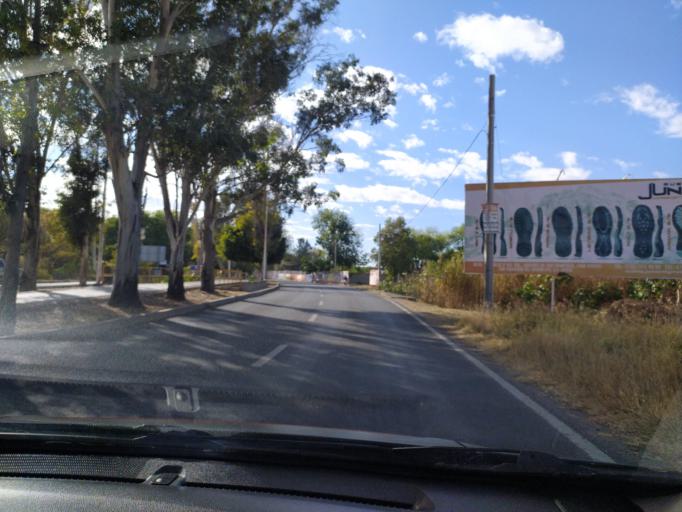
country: LA
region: Oudomxai
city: Muang La
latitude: 21.0322
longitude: 101.8354
